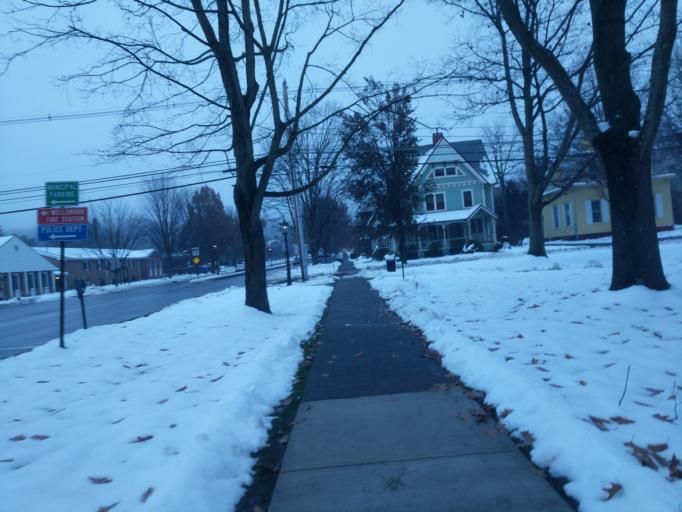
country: US
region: Pennsylvania
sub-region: Tioga County
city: Wellsboro
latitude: 41.7471
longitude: -77.3016
